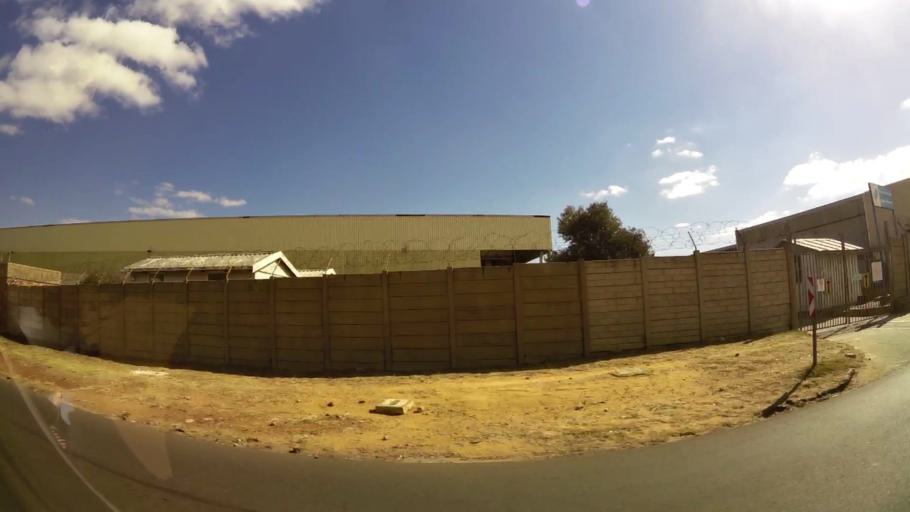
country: ZA
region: Gauteng
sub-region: West Rand District Municipality
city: Krugersdorp
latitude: -26.1142
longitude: 27.8096
